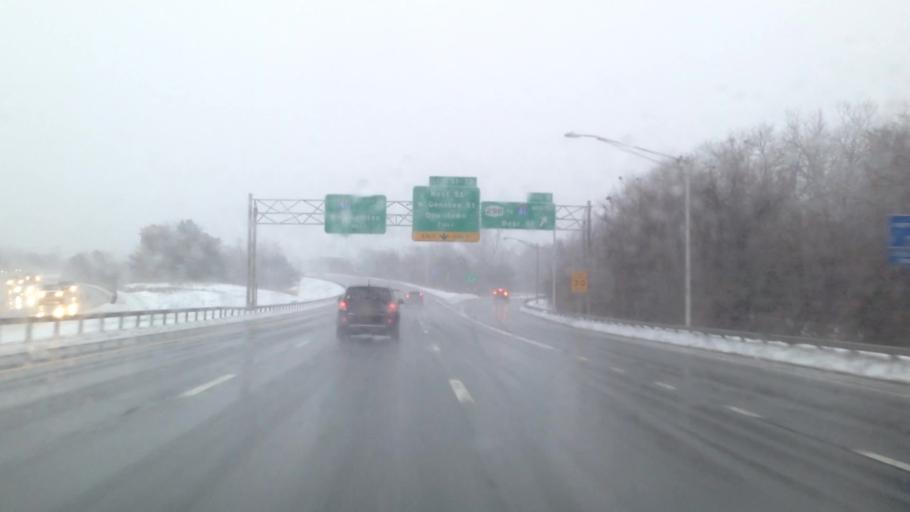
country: US
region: New York
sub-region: Onondaga County
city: Solvay
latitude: 43.0575
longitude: -76.1809
